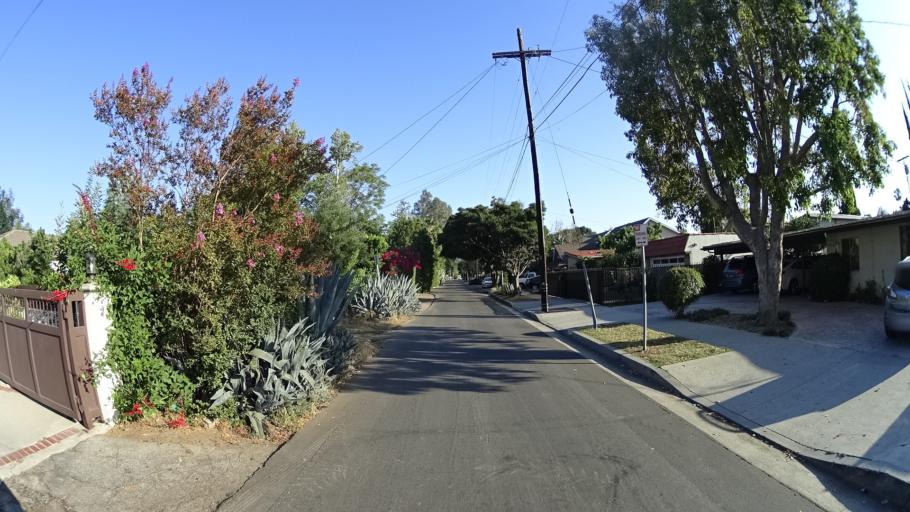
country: US
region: California
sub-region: Los Angeles County
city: Van Nuys
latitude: 34.1717
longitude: -118.4421
